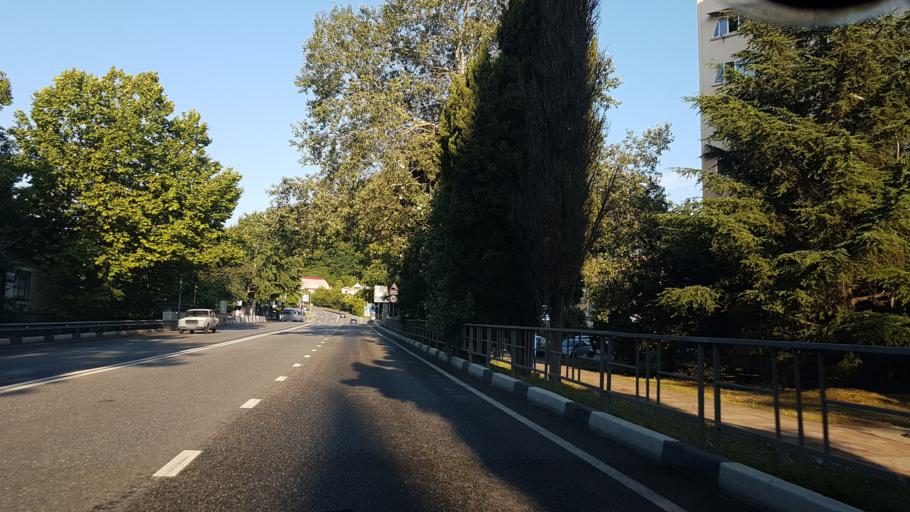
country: RU
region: Krasnodarskiy
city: Dagomys
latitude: 43.6595
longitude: 39.6536
